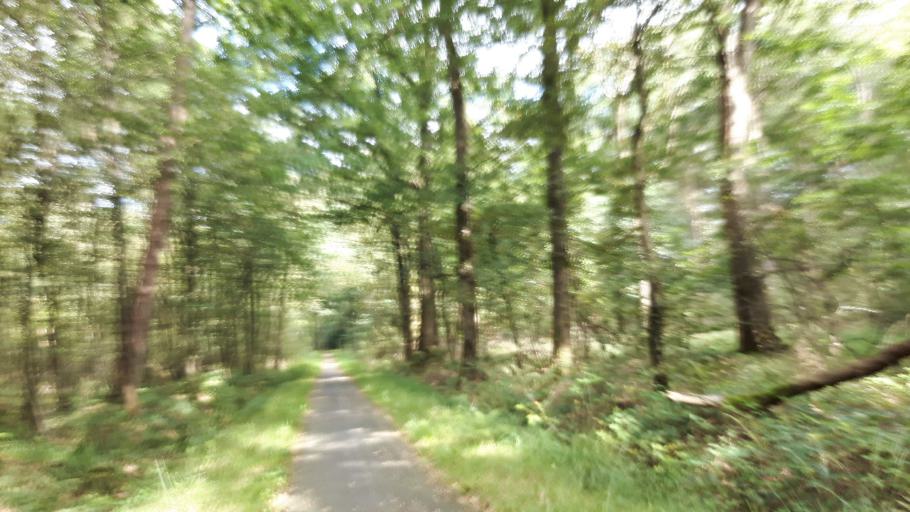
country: NL
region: Friesland
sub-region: Gemeente Smallingerland
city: Drachtstercompagnie
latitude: 53.0679
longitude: 6.2092
